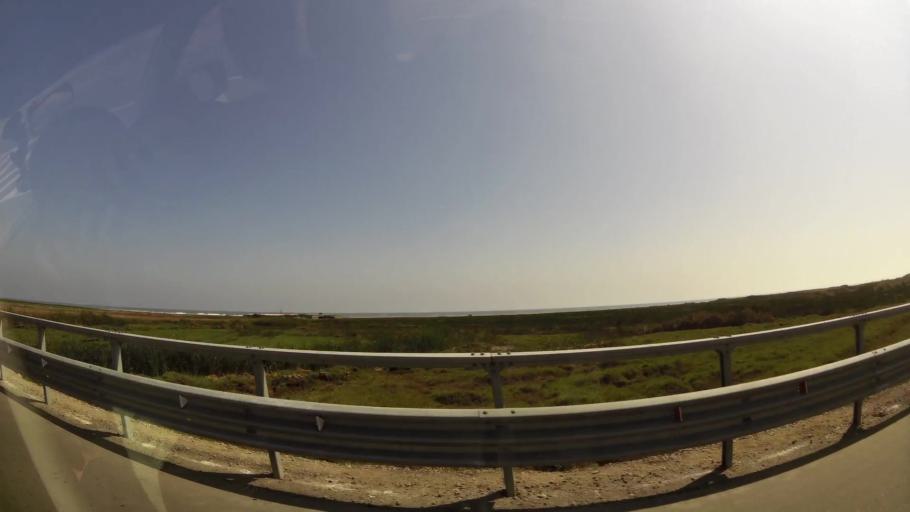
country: PE
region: Ica
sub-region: Provincia de Chincha
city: Sunampe
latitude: -13.4090
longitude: -76.1925
